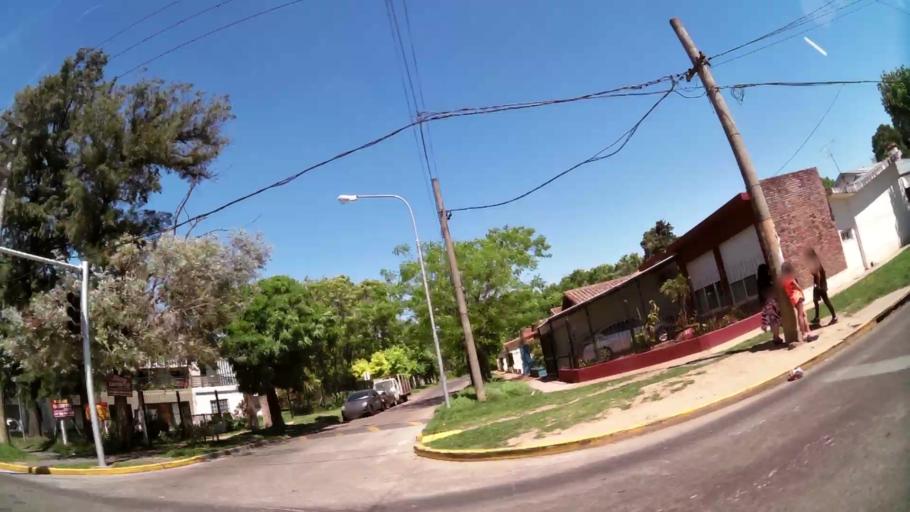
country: AR
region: Buenos Aires
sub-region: Partido de Tigre
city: Tigre
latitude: -34.4881
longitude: -58.6472
